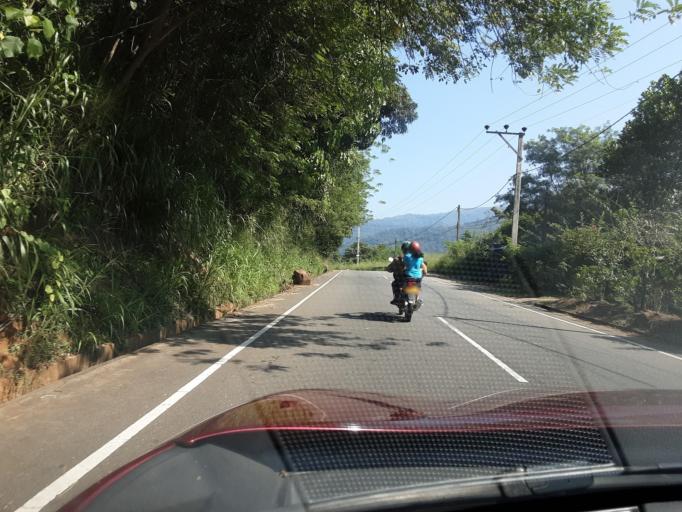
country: LK
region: Uva
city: Badulla
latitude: 7.0341
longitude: 81.0577
